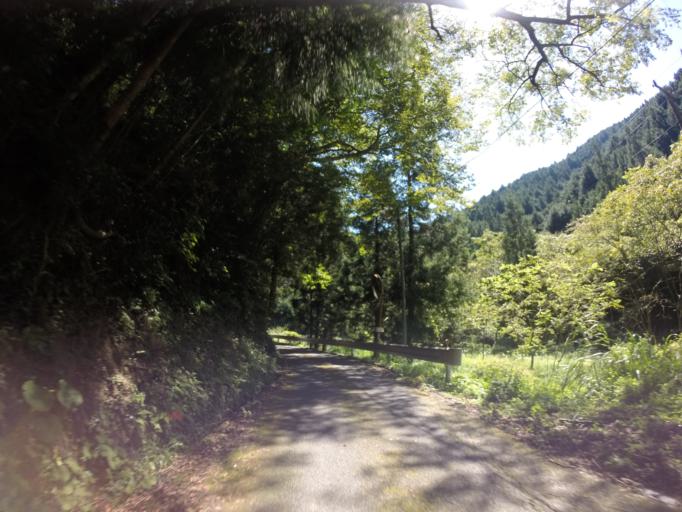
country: JP
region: Shizuoka
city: Fujieda
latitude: 34.9515
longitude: 138.1639
